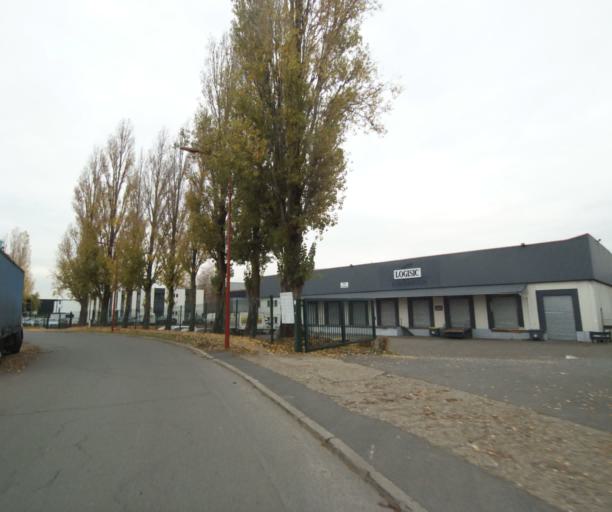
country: FR
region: Ile-de-France
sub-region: Departement du Val-d'Oise
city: Gonesse
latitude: 48.9824
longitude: 2.4651
